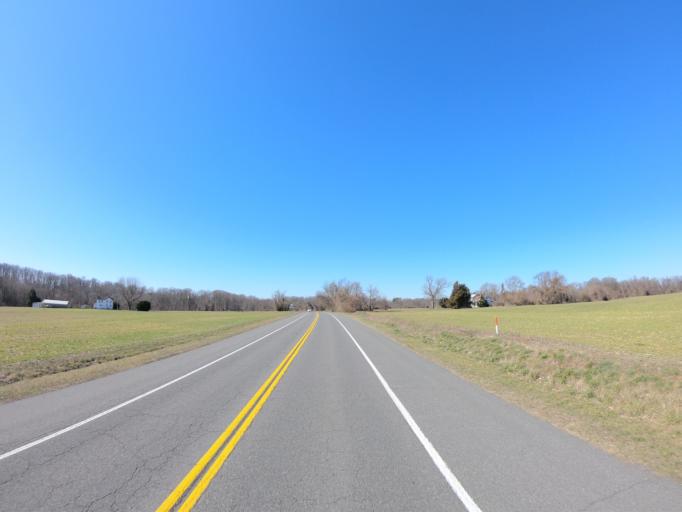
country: US
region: Delaware
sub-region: New Castle County
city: Townsend
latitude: 39.3437
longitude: -75.8598
